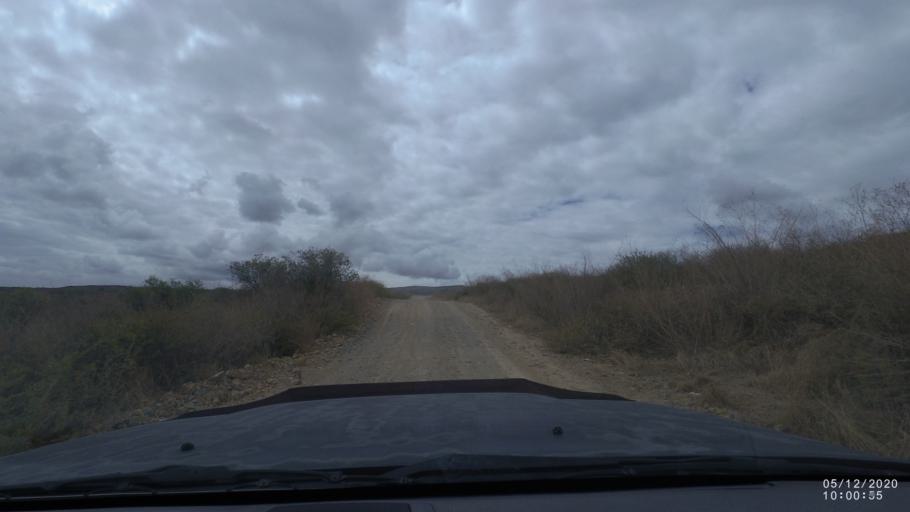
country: BO
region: Cochabamba
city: Sipe Sipe
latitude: -17.4391
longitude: -66.2851
